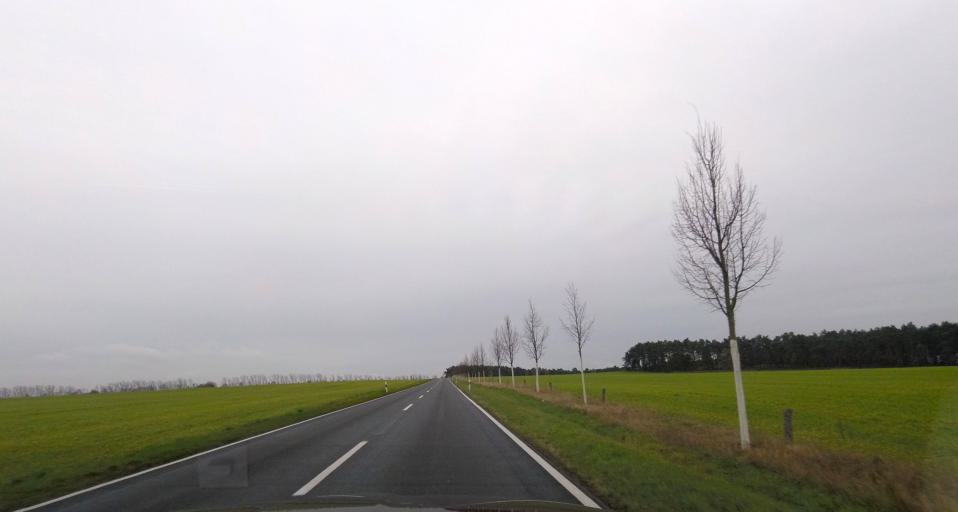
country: DE
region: Brandenburg
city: Niemegk
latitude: 52.0424
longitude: 12.7141
